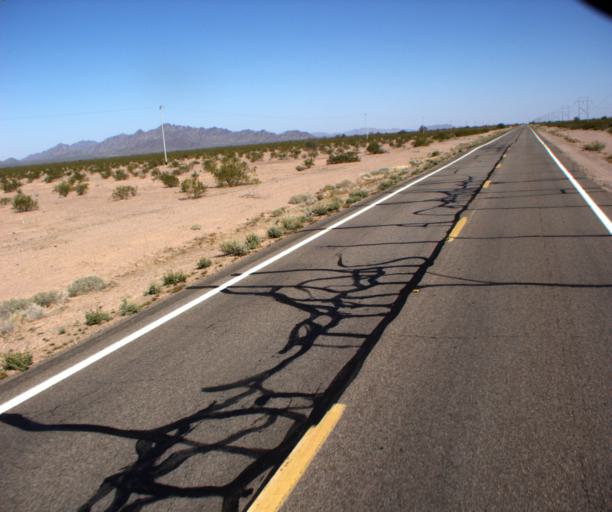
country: US
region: Arizona
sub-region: La Paz County
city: Quartzsite
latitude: 33.4195
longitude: -114.2170
